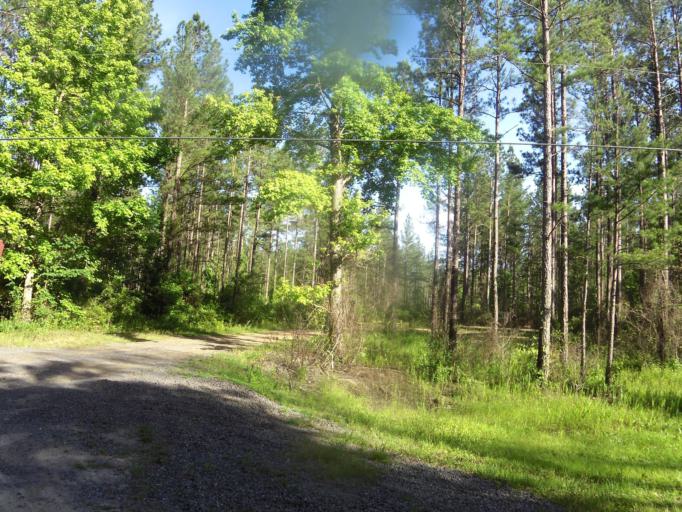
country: US
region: Florida
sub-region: Nassau County
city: Nassau Village-Ratliff
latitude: 30.4598
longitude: -81.8257
